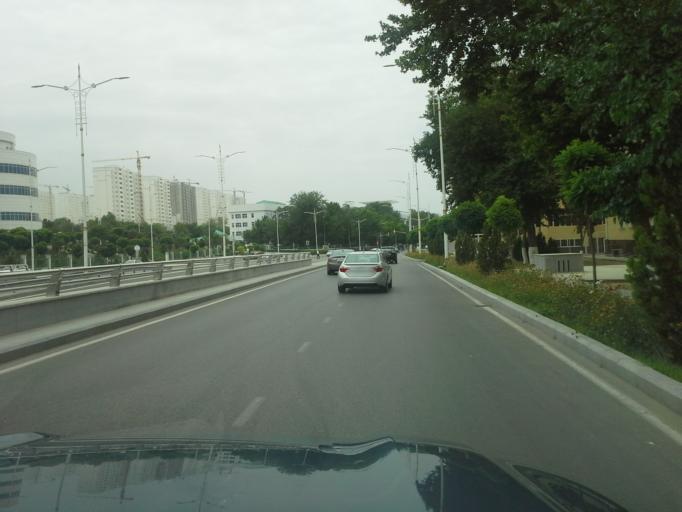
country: TM
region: Ahal
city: Ashgabat
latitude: 37.9429
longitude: 58.3628
